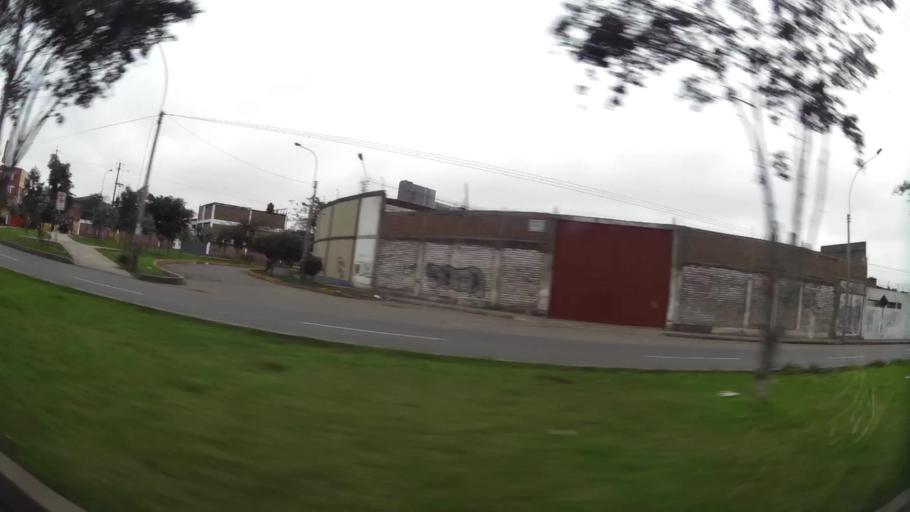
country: PE
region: Lima
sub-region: Lima
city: San Luis
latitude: -12.0634
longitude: -76.9781
